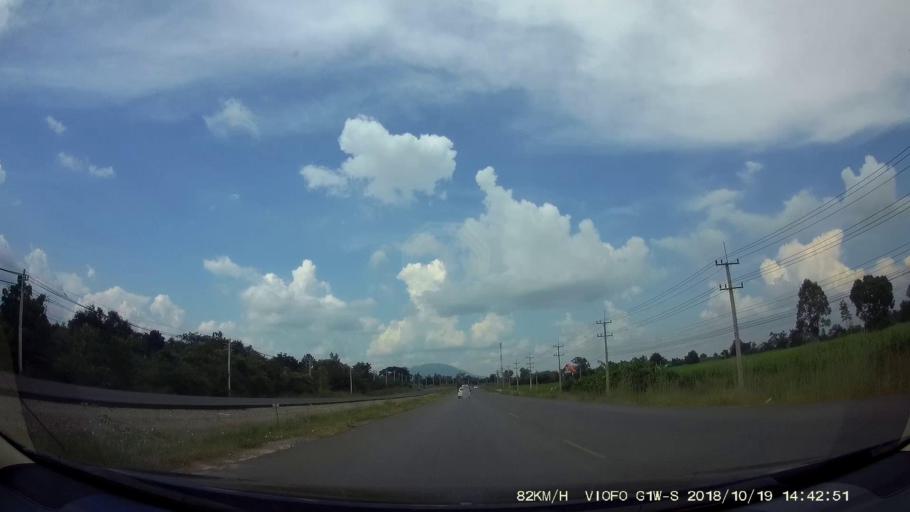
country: TH
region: Chaiyaphum
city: Phu Khiao
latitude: 16.2732
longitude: 102.2044
